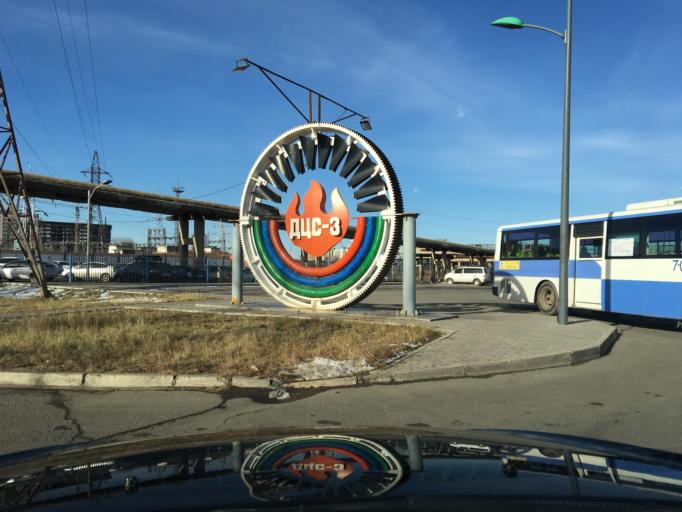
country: MN
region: Ulaanbaatar
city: Ulaanbaatar
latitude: 47.8991
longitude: 106.8680
